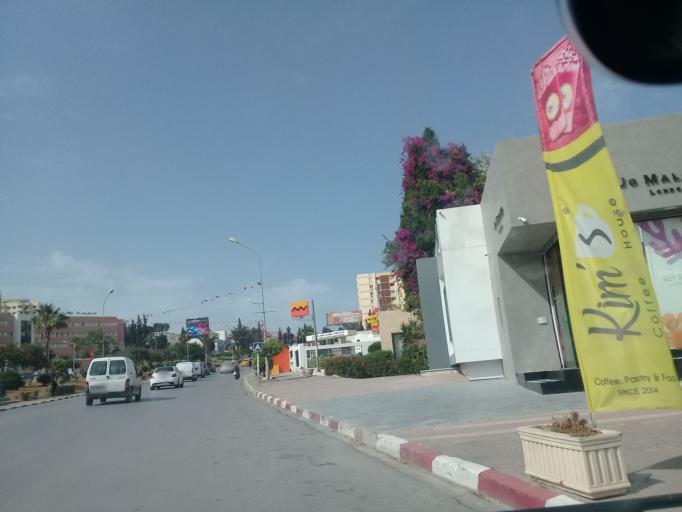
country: TN
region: Tunis
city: Tunis
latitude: 36.8461
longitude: 10.1673
